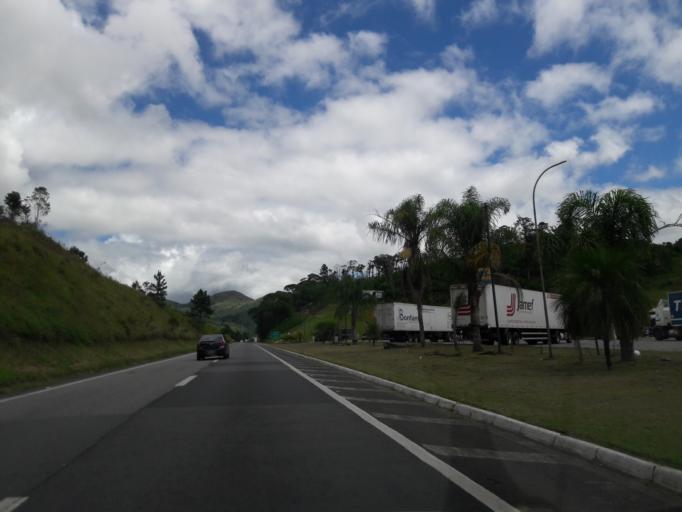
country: BR
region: Parana
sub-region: Campina Grande Do Sul
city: Campina Grande do Sul
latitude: -25.1081
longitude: -48.7934
